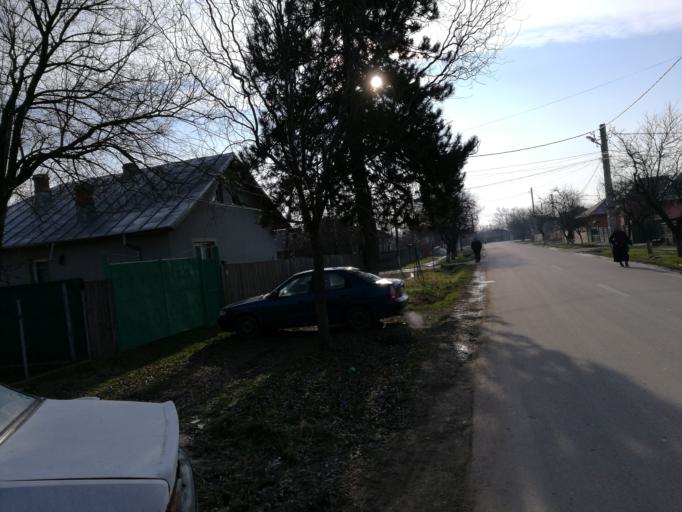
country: RO
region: Ialomita
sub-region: Comuna Fierbinti-Targ
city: Fierbintii de Jos
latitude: 44.6948
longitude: 26.3948
